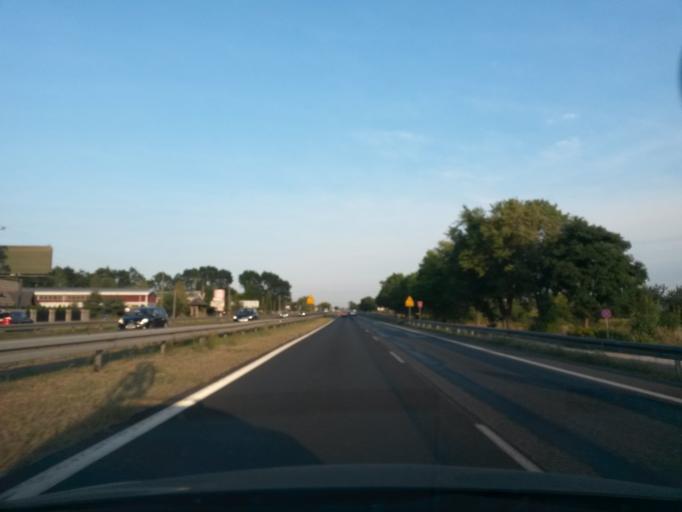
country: PL
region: Masovian Voivodeship
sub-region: Powiat warszawski zachodni
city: Dziekanow Lesny
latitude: 52.3632
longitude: 20.8175
